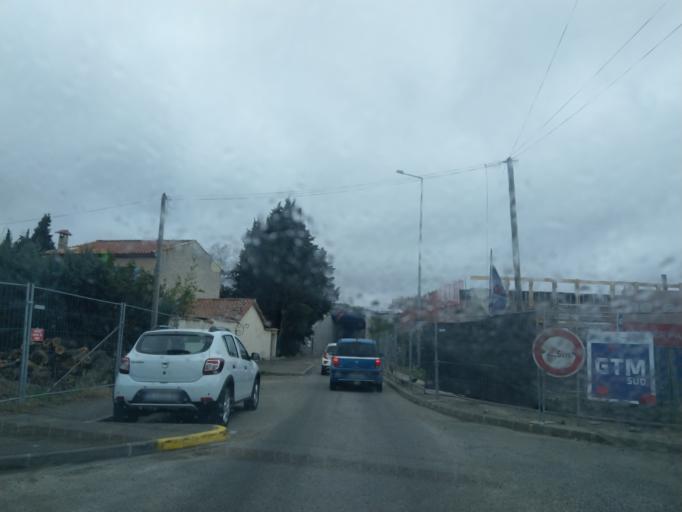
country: FR
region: Provence-Alpes-Cote d'Azur
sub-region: Departement des Bouches-du-Rhone
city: Septemes-les-Vallons
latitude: 43.4136
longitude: 5.3657
